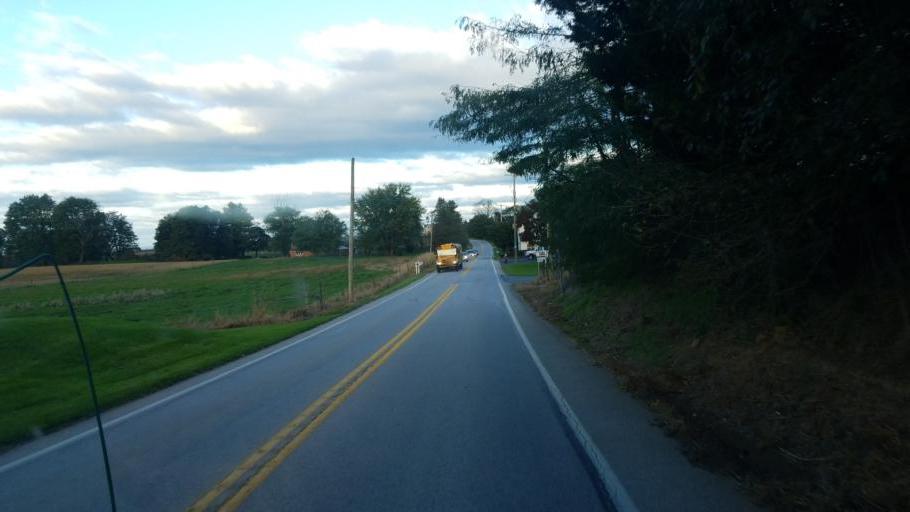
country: US
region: Pennsylvania
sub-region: Adams County
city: East Berlin
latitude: 39.9356
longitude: -76.9399
